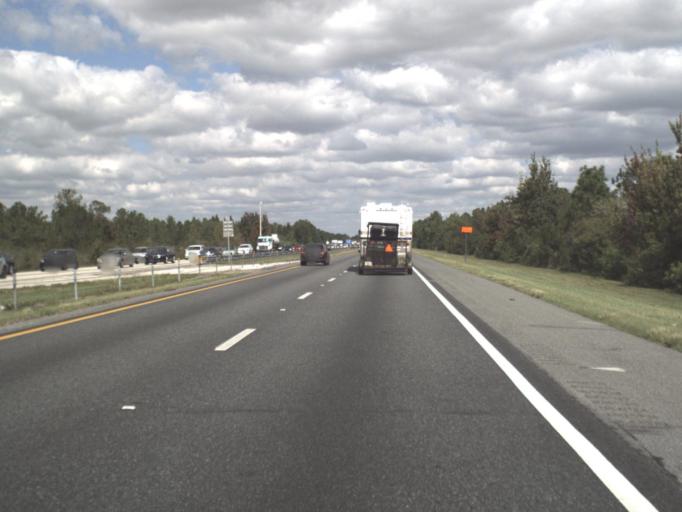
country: US
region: Florida
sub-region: Orange County
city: Southchase
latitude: 28.3953
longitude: -81.3912
